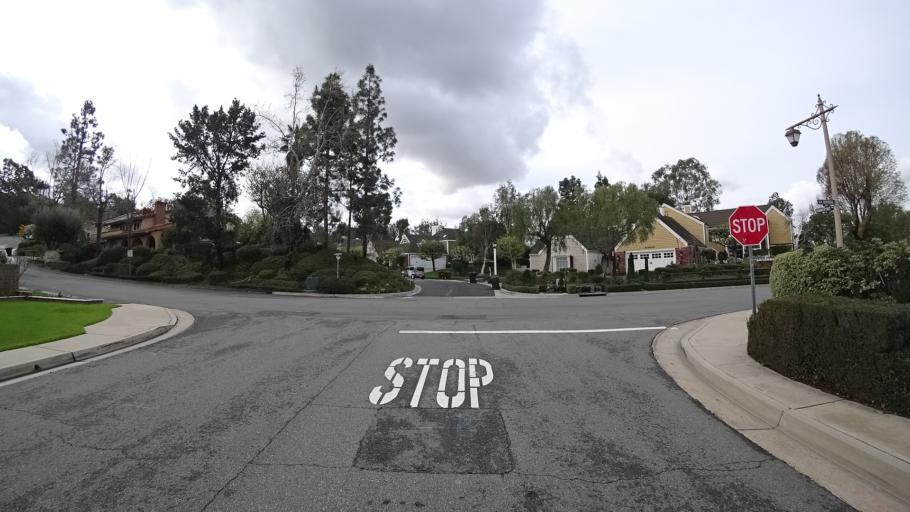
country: US
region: California
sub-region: Orange County
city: Villa Park
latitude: 33.8511
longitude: -117.7777
